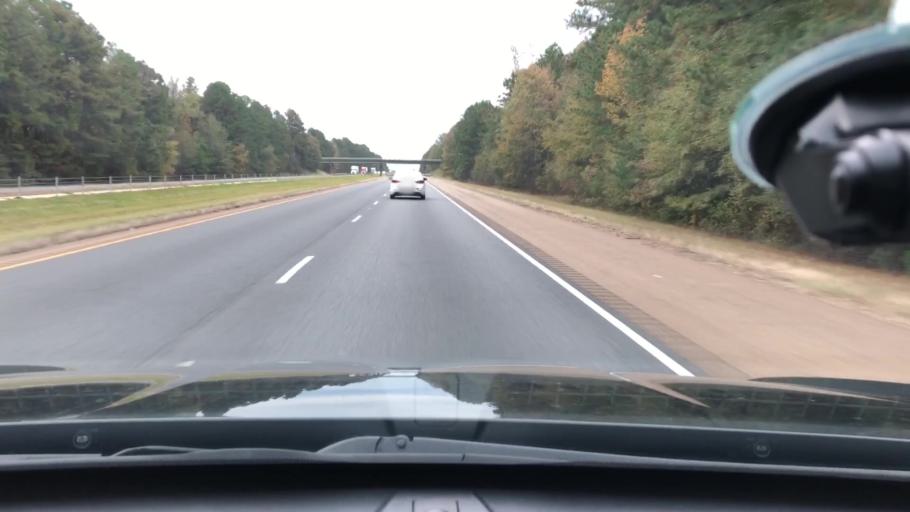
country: US
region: Arkansas
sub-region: Clark County
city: Gurdon
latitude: 33.9692
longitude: -93.2110
